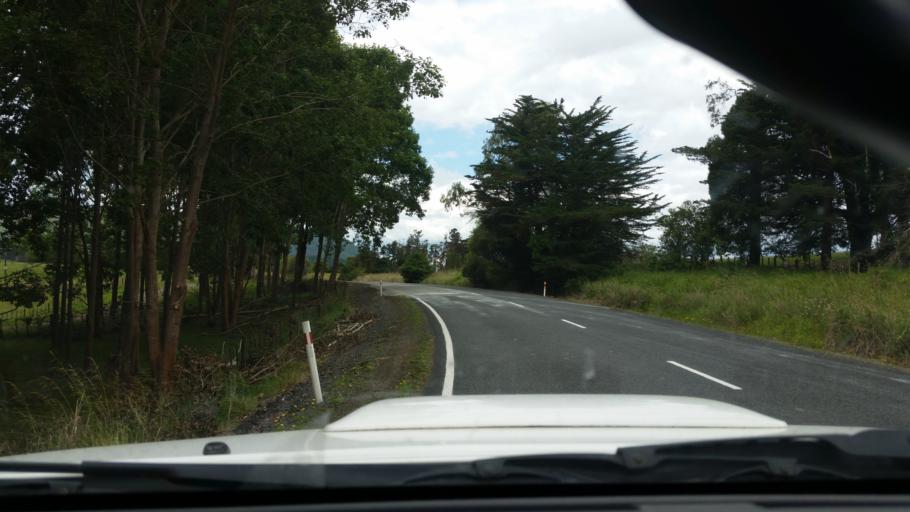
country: NZ
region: Northland
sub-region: Kaipara District
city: Dargaville
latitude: -35.7502
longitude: 173.8880
